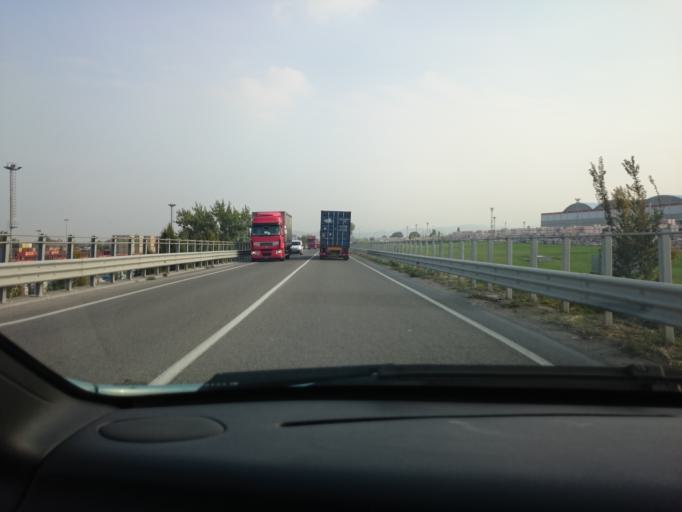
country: IT
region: Emilia-Romagna
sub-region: Provincia di Reggio Emilia
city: Veggia-Villalunga
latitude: 44.5706
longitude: 10.7516
